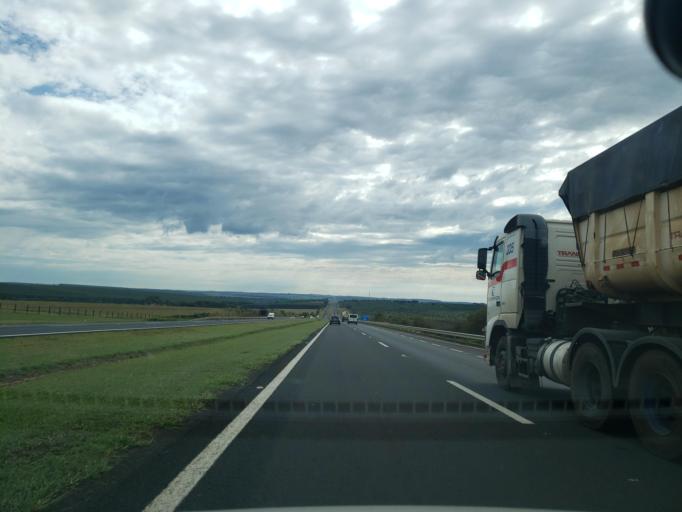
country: BR
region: Sao Paulo
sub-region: Bauru
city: Bauru
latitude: -22.1853
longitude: -49.2145
